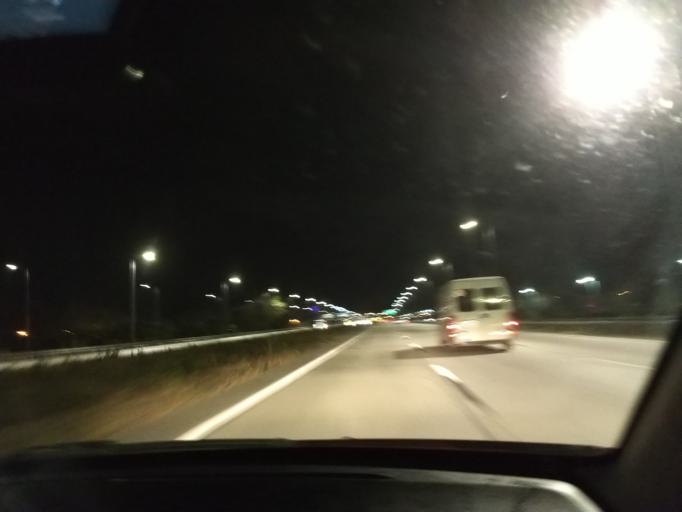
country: AR
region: Cordoba
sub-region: Departamento de Capital
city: Cordoba
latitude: -31.3829
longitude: -64.2600
